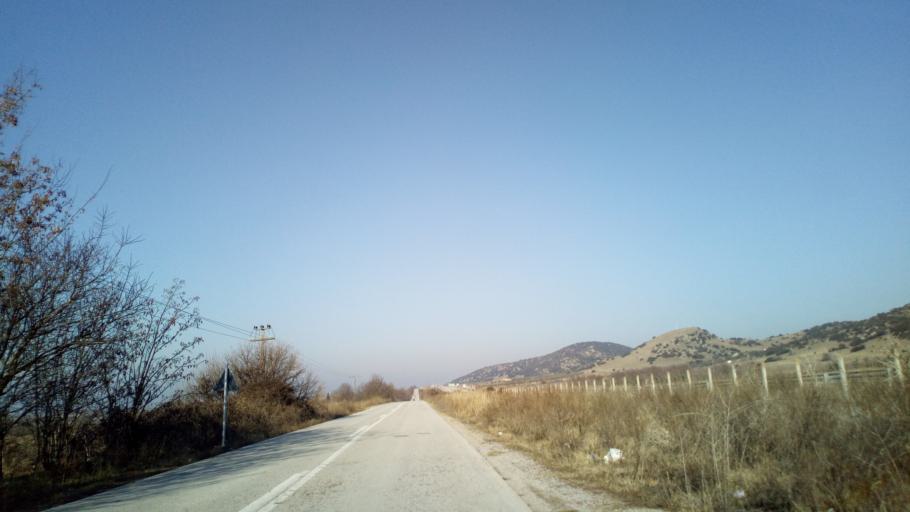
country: GR
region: Central Macedonia
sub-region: Nomos Thessalonikis
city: Gerakarou
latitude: 40.6986
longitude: 23.2068
